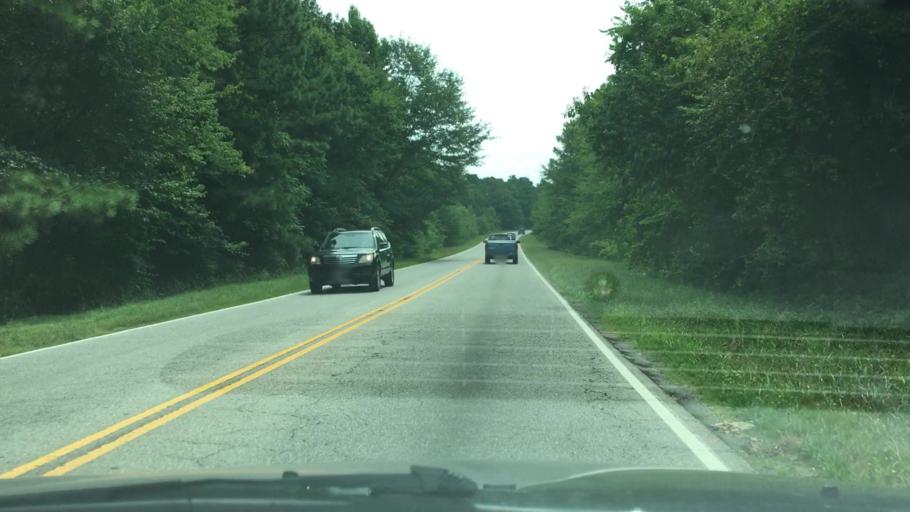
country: US
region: South Carolina
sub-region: Aiken County
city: Warrenville
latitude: 33.5295
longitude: -81.7601
